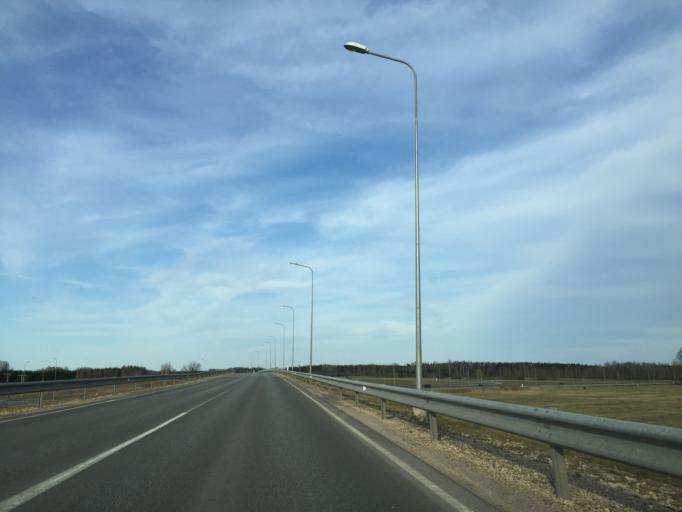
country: LV
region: Lielvarde
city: Lielvarde
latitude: 56.8058
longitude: 24.8785
